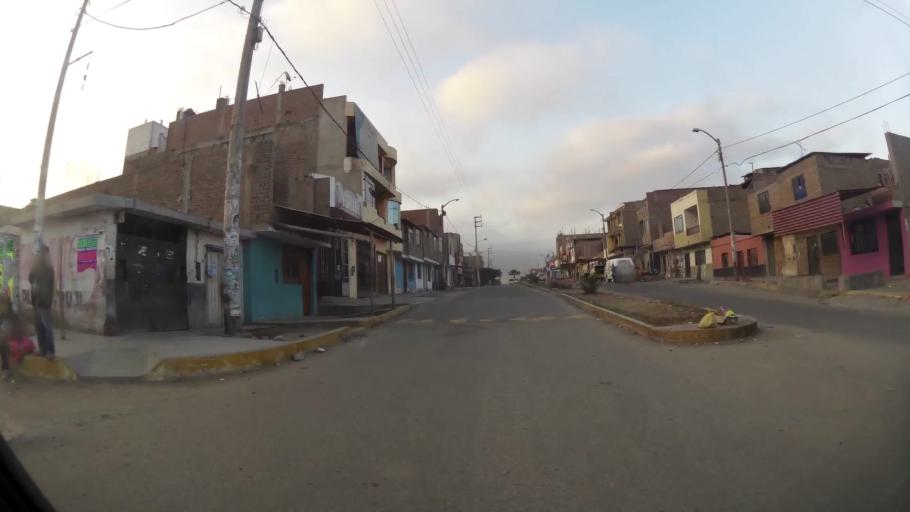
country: PE
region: La Libertad
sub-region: Provincia de Trujillo
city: El Porvenir
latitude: -8.0736
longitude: -78.9982
